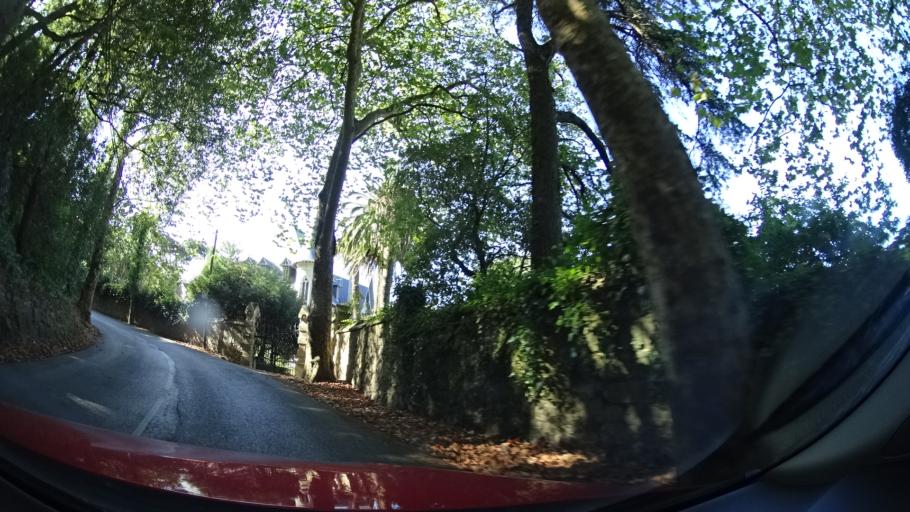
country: PT
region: Lisbon
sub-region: Sintra
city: Sintra
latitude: 38.7945
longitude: -9.3950
